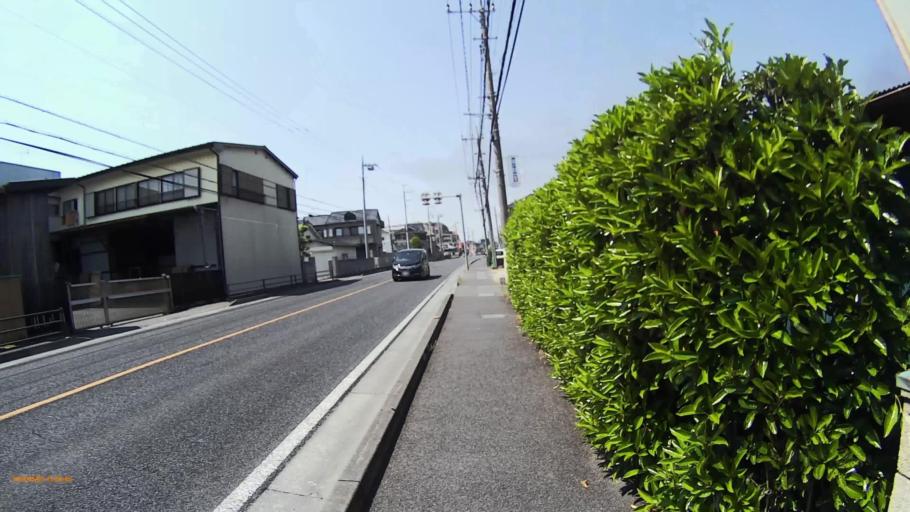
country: JP
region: Saitama
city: Kasukabe
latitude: 35.9622
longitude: 139.7722
